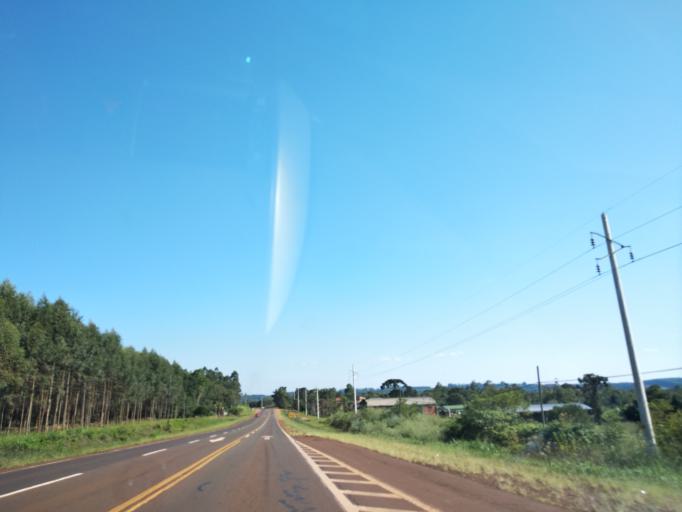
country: AR
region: Misiones
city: Puerto Rico
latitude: -26.8462
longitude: -55.0419
